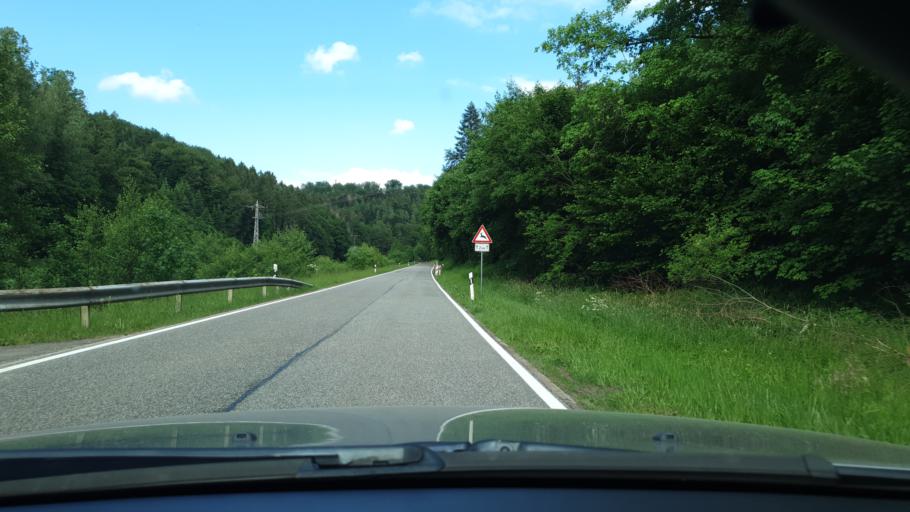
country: DE
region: Rheinland-Pfalz
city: Battweiler
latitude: 49.2801
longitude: 7.4759
